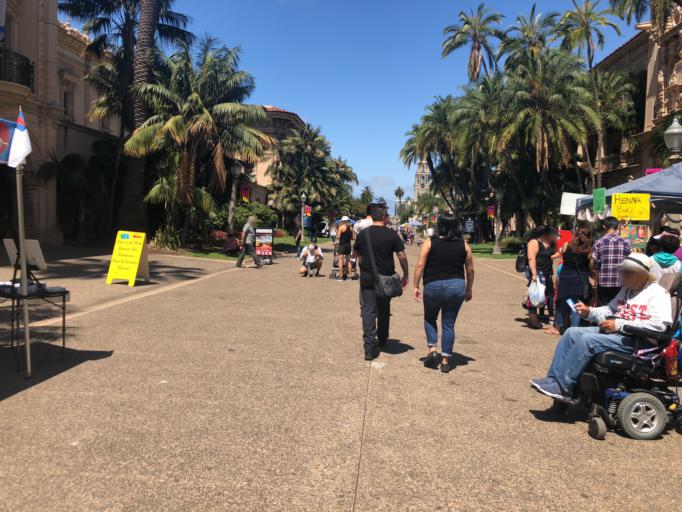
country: US
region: California
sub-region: San Diego County
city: San Diego
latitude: 32.7315
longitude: -117.1481
